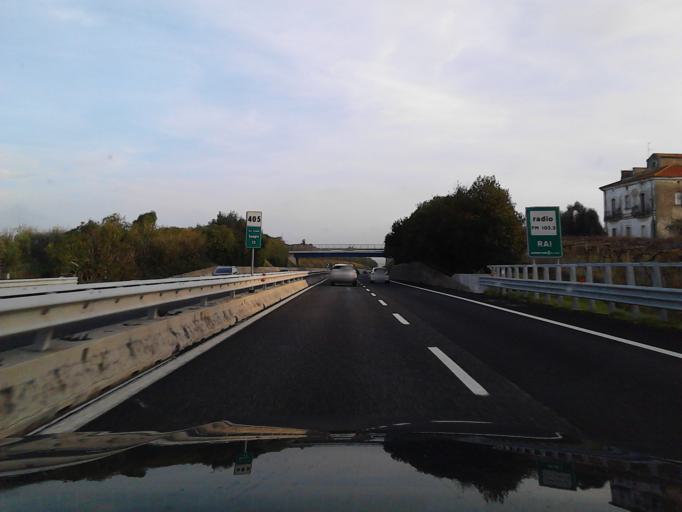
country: IT
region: Abruzzo
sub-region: Provincia di Chieti
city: Ortona
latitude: 42.3238
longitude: 14.3933
